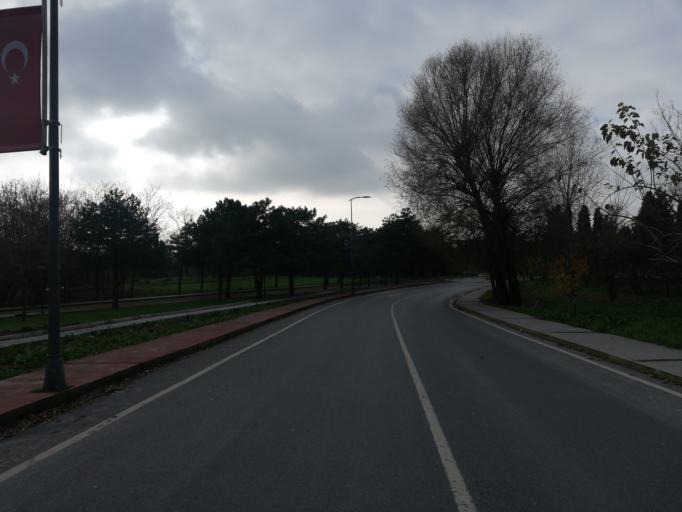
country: TR
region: Istanbul
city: merter keresteciler
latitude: 41.0237
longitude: 28.8936
